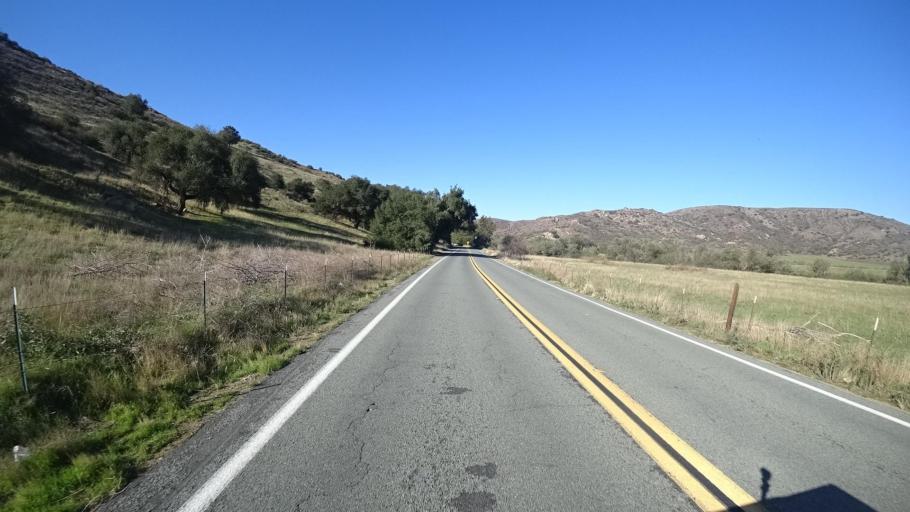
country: US
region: California
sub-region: San Diego County
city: Jamul
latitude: 32.6673
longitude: -116.8308
